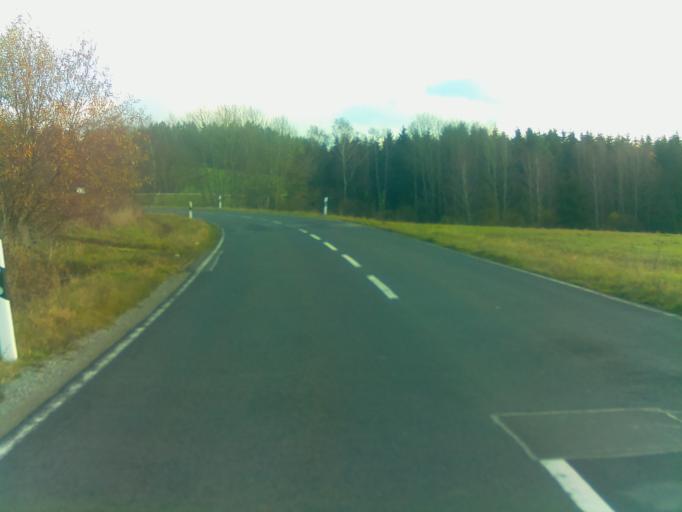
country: DE
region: Thuringia
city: Schleusingen
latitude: 50.4716
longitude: 10.7564
